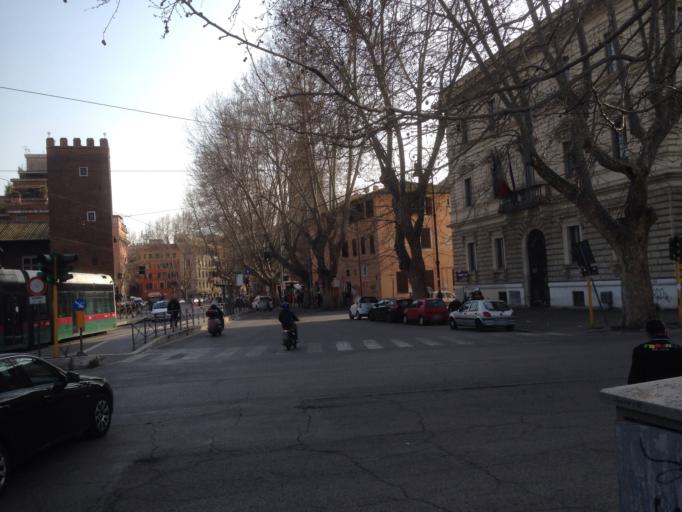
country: VA
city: Vatican City
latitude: 41.8905
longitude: 12.4743
